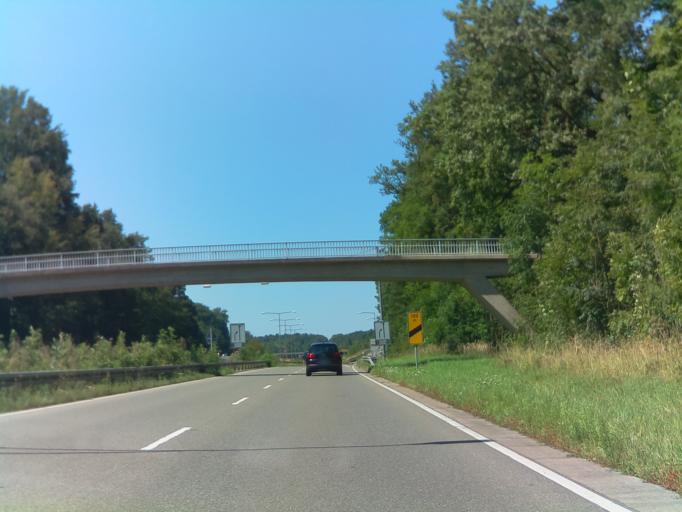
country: DE
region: Baden-Wuerttemberg
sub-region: Regierungsbezirk Stuttgart
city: Gerlingen
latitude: 48.7757
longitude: 9.0953
